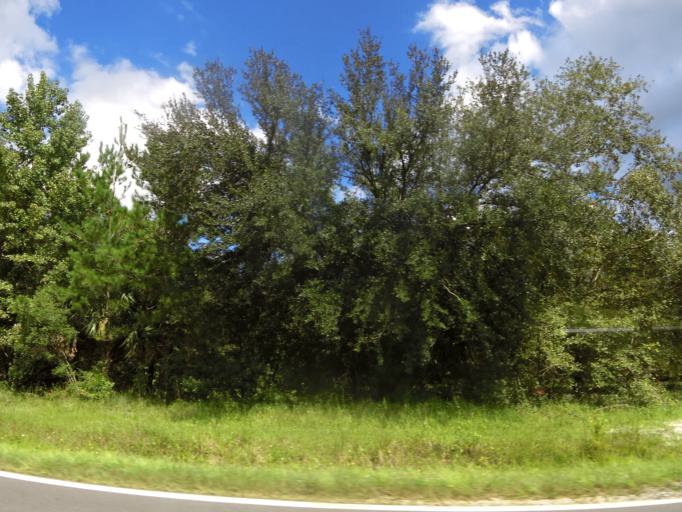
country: US
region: Florida
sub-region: Saint Johns County
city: Saint Augustine
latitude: 29.9406
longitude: -81.4941
